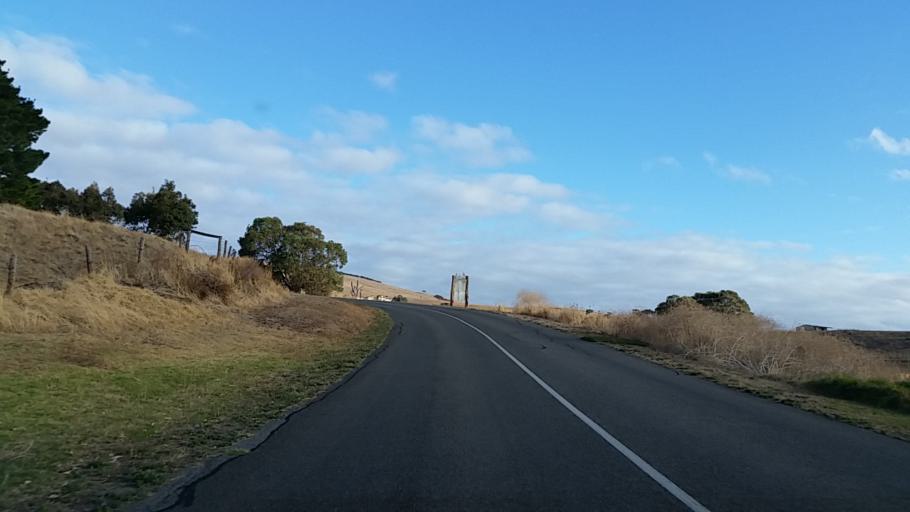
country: AU
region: South Australia
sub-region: Yankalilla
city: Normanville
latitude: -35.5092
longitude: 138.2616
